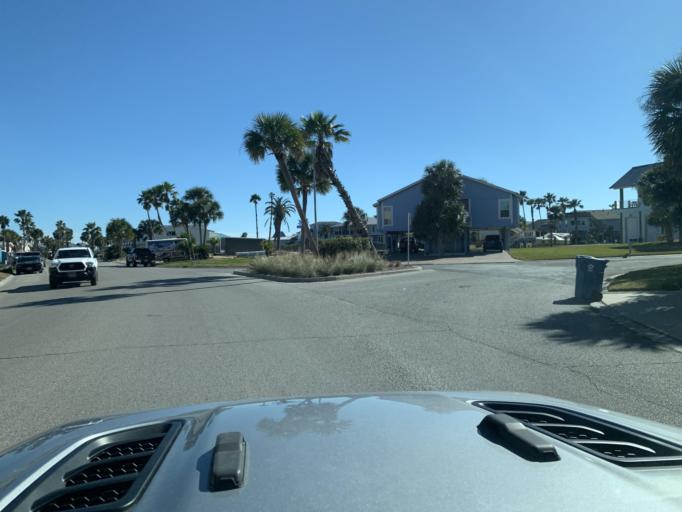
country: US
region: Texas
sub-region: Aransas County
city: Fulton
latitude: 28.0420
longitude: -97.0268
